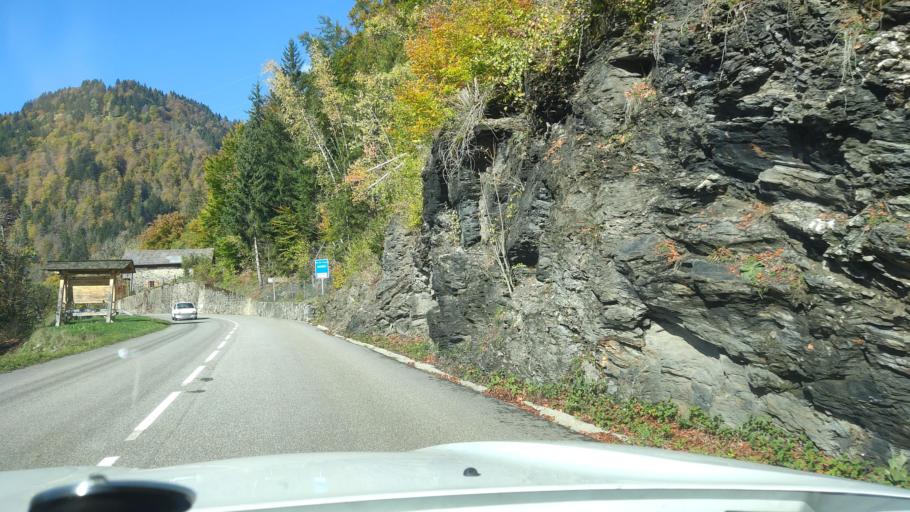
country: FR
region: Rhone-Alpes
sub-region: Departement de la Haute-Savoie
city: Praz-sur-Arly
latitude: 45.8220
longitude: 6.5138
